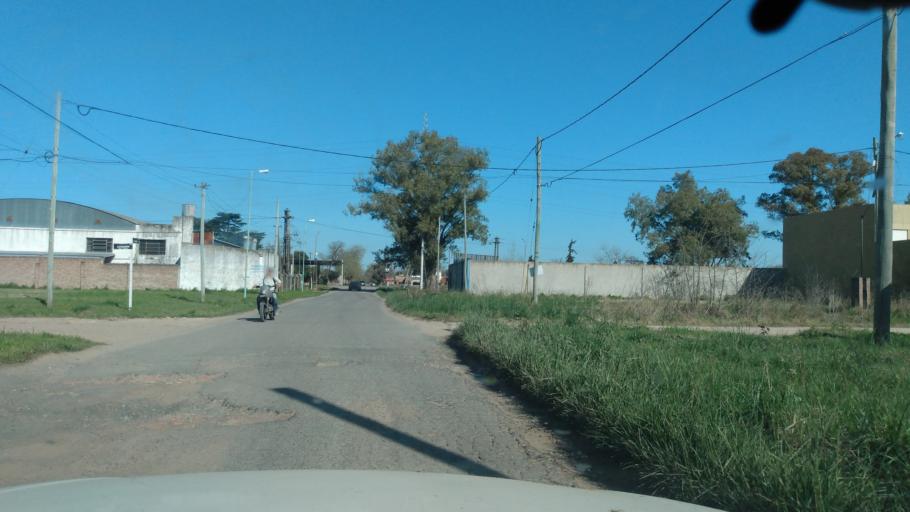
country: AR
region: Buenos Aires
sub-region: Partido de Lujan
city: Lujan
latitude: -34.5801
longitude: -59.0968
